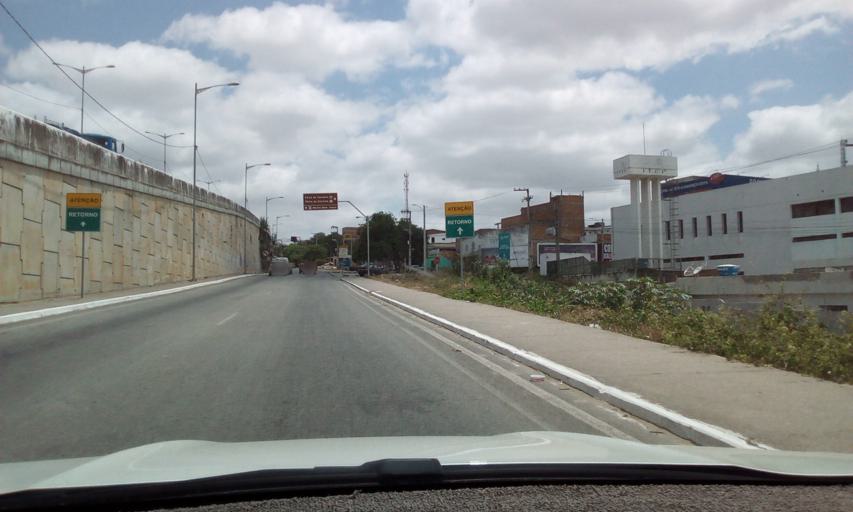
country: BR
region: Pernambuco
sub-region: Caruaru
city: Caruaru
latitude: -8.2894
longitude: -35.9844
